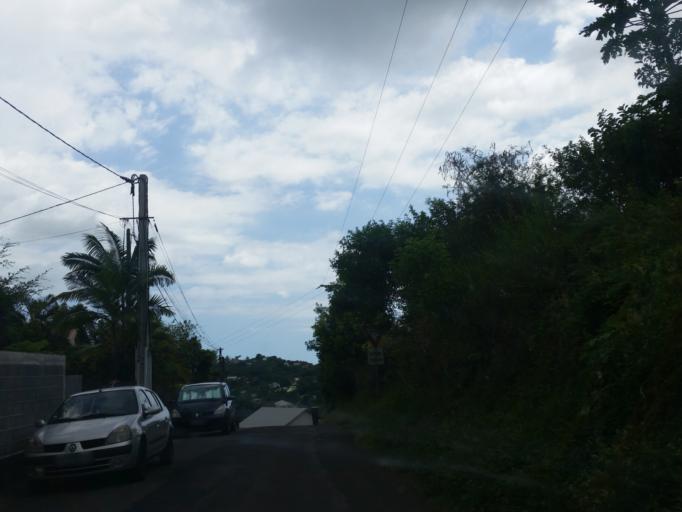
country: RE
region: Reunion
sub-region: Reunion
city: L'Entre-Deux
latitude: -21.2442
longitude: 55.4678
